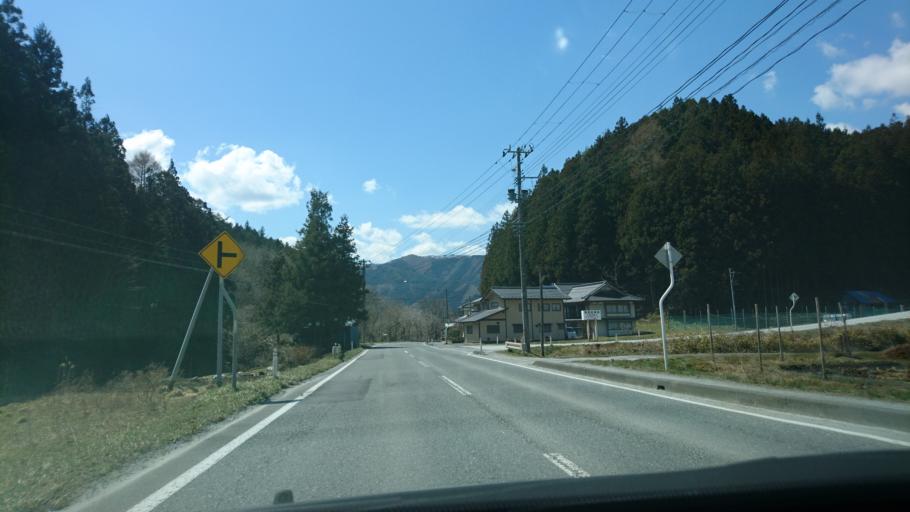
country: JP
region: Iwate
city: Ofunato
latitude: 39.1447
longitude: 141.5973
